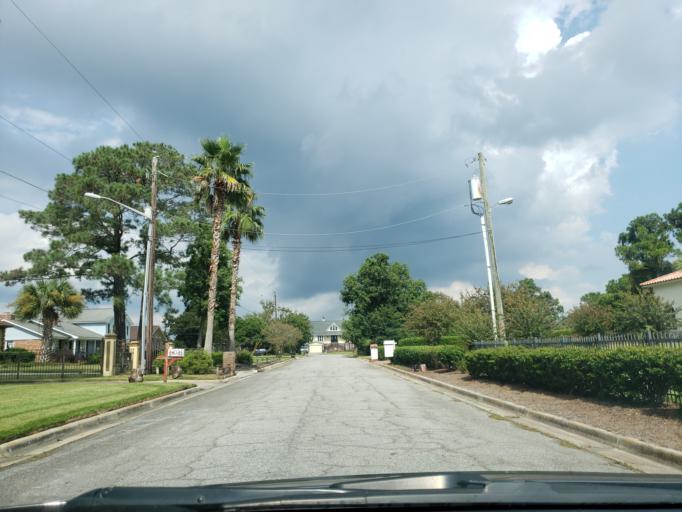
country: US
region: Georgia
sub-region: Chatham County
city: Skidaway Island
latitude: 31.9283
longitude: -81.0828
